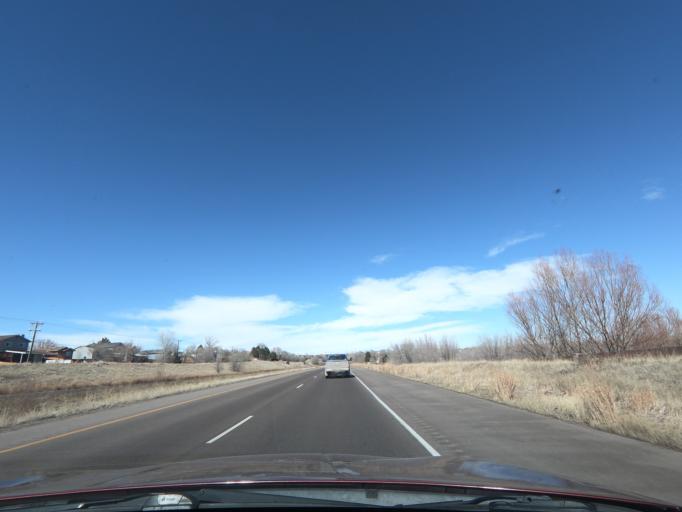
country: US
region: Colorado
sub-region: El Paso County
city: Security-Widefield
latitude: 38.7267
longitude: -104.6825
